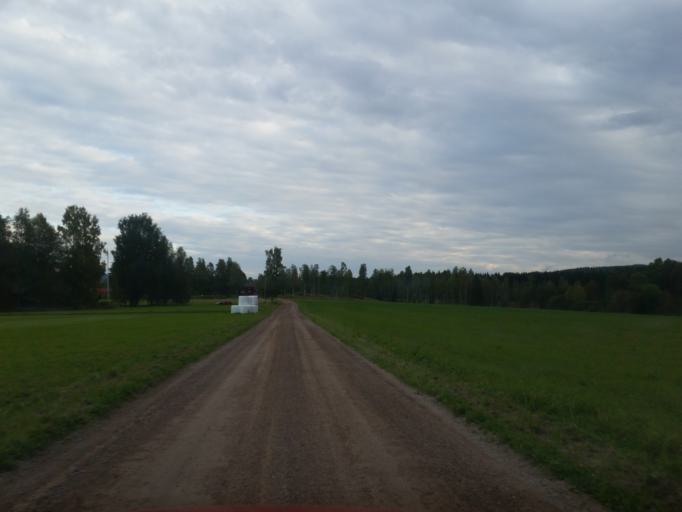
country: SE
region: Dalarna
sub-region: Leksand Municipality
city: Smedby
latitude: 60.6782
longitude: 15.1385
